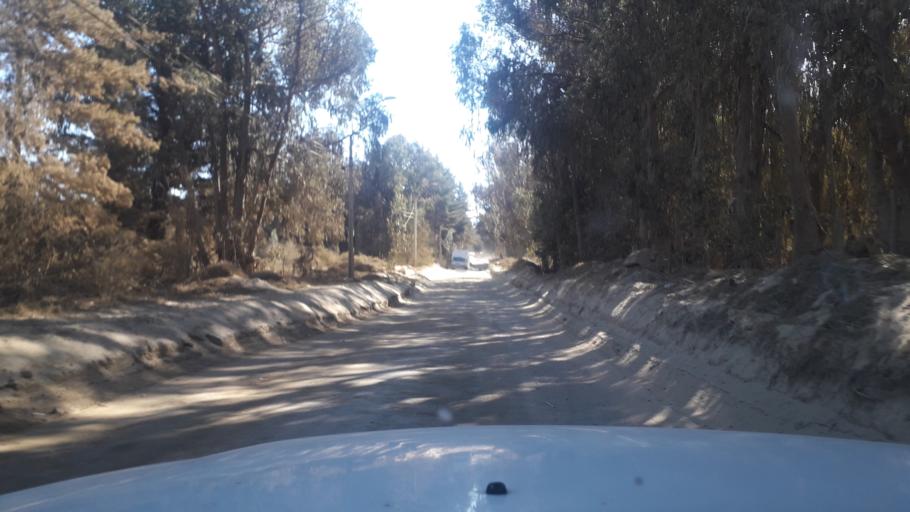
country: CL
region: Valparaiso
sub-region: Provincia de Valparaiso
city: Vina del Mar
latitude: -32.9574
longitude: -71.5173
